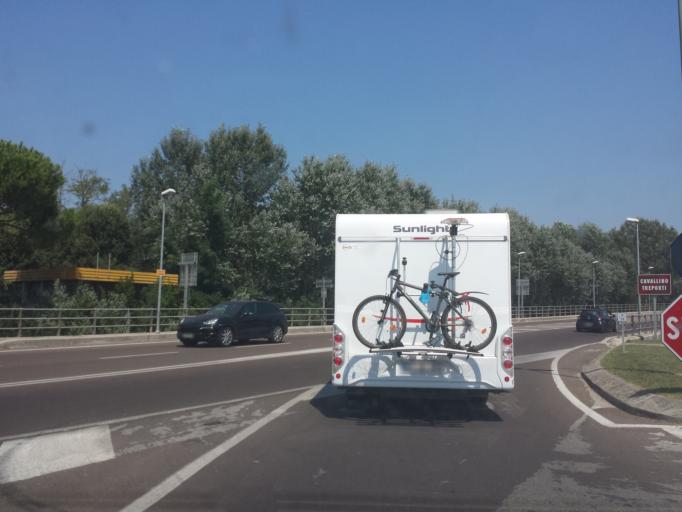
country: IT
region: Veneto
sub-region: Provincia di Venezia
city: Cavallino
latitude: 45.4880
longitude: 12.5764
